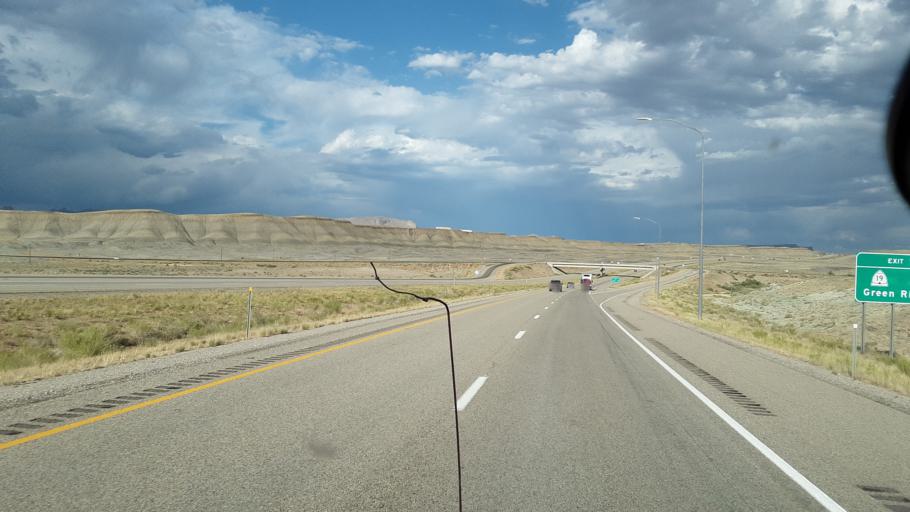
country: US
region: Utah
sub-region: Carbon County
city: East Carbon City
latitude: 38.9752
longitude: -110.1282
